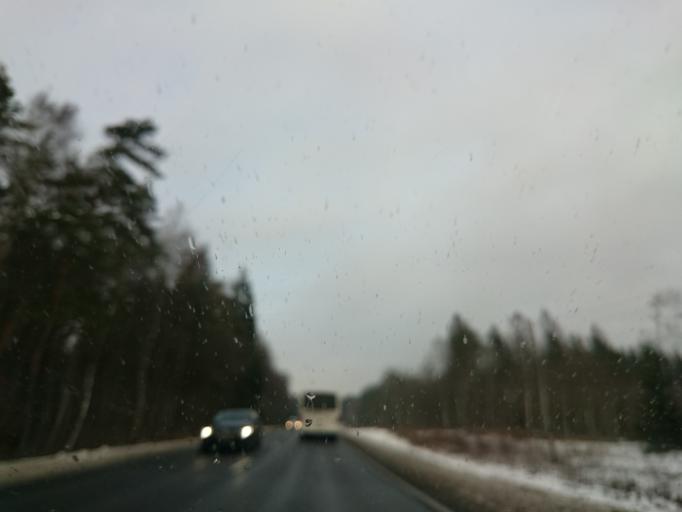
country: LV
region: Pargaujas
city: Stalbe
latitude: 57.3045
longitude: 24.9251
